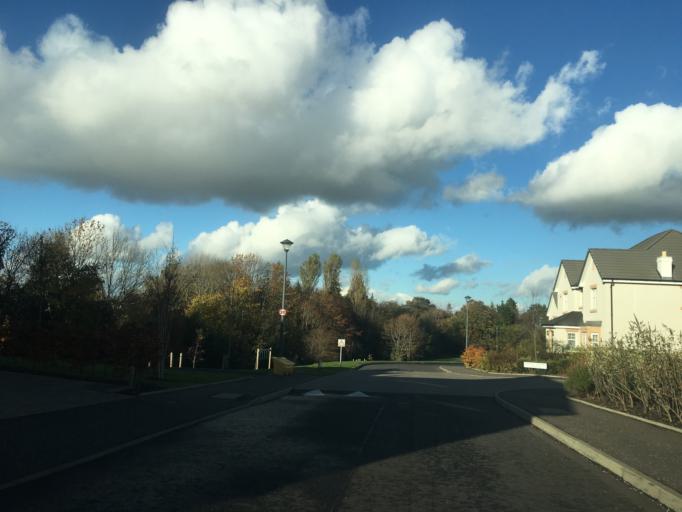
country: GB
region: Scotland
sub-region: Edinburgh
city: Colinton
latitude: 55.8995
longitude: -3.2502
